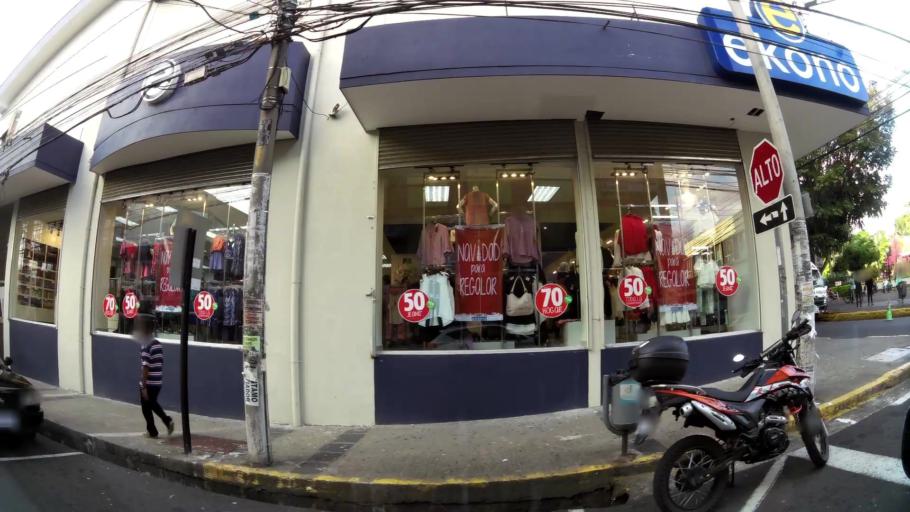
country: CR
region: Heredia
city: Heredia
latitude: 9.9981
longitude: -84.1176
